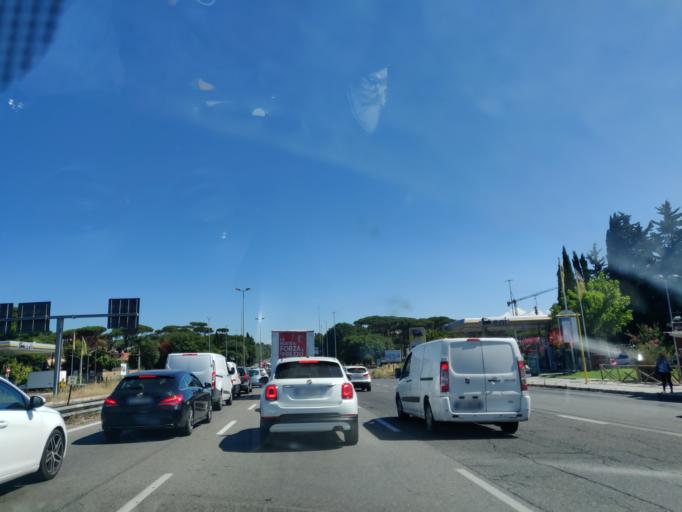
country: IT
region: Latium
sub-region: Citta metropolitana di Roma Capitale
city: Selcetta
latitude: 41.8168
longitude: 12.4622
